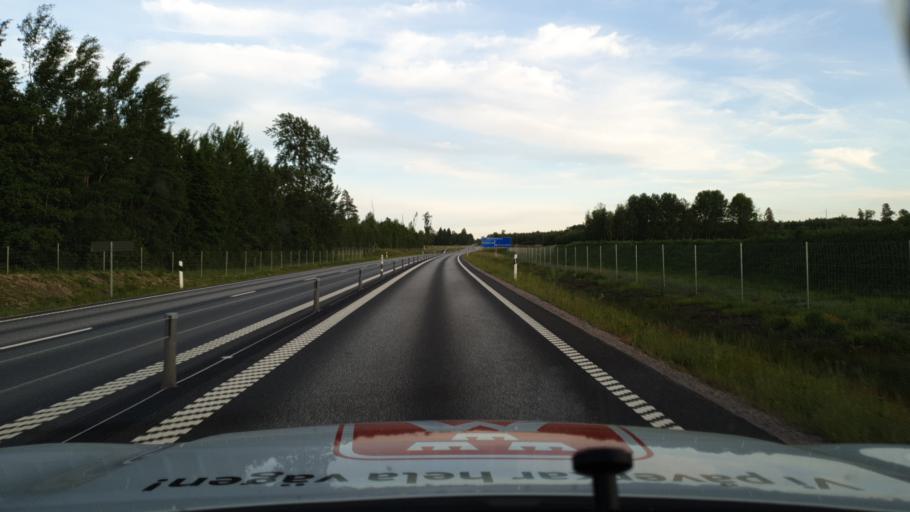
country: SE
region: OErebro
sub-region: Hallsbergs Kommun
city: Palsboda
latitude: 59.0855
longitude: 15.3086
